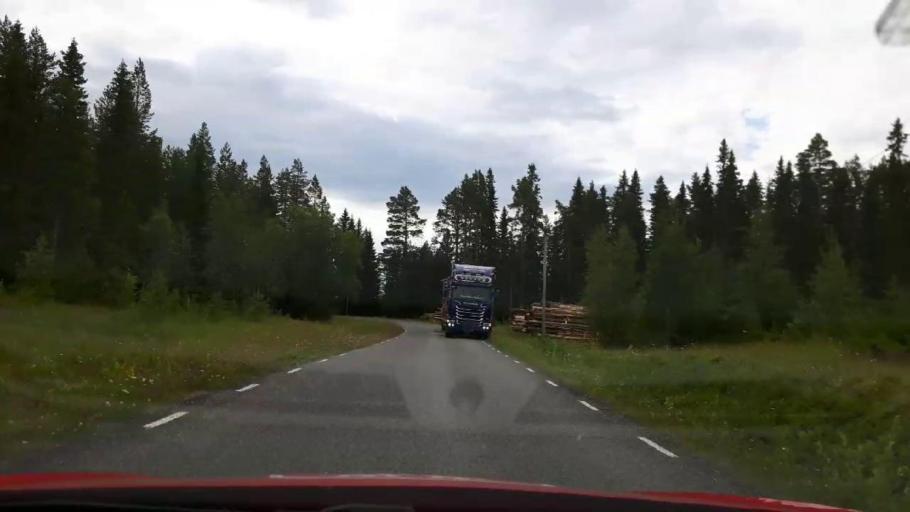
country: SE
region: Jaemtland
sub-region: OEstersunds Kommun
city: Lit
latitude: 63.3911
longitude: 15.0136
